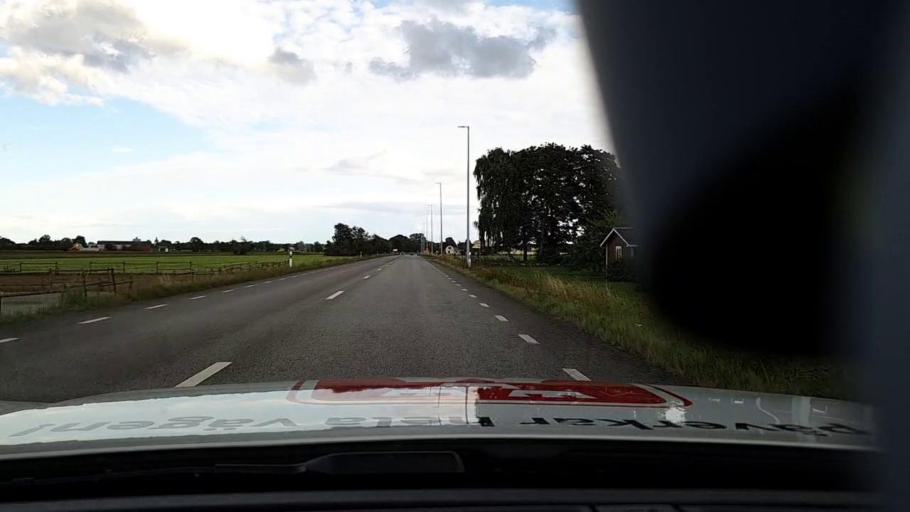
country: SE
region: Blekinge
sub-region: Solvesborgs Kommun
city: Soelvesborg
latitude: 56.0529
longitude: 14.6447
